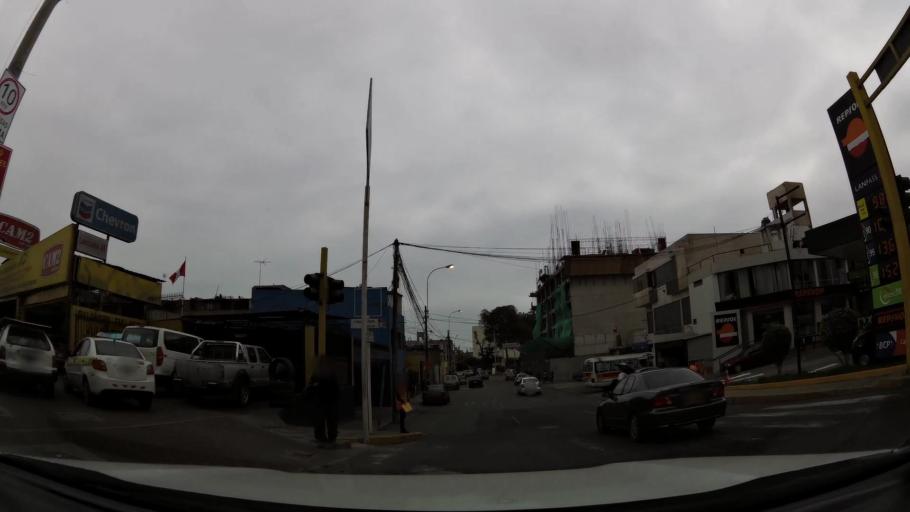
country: PE
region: Lima
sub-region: Lima
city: Surco
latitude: -12.1390
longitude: -77.0178
